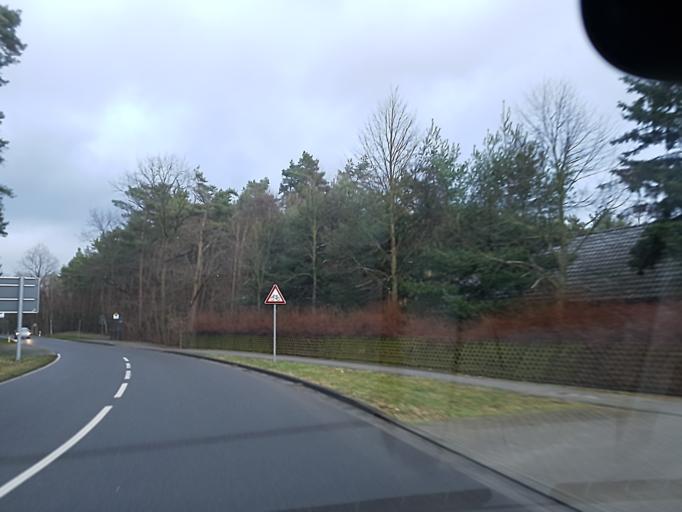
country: DE
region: Brandenburg
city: Elsterwerda
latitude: 51.4791
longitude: 13.5057
